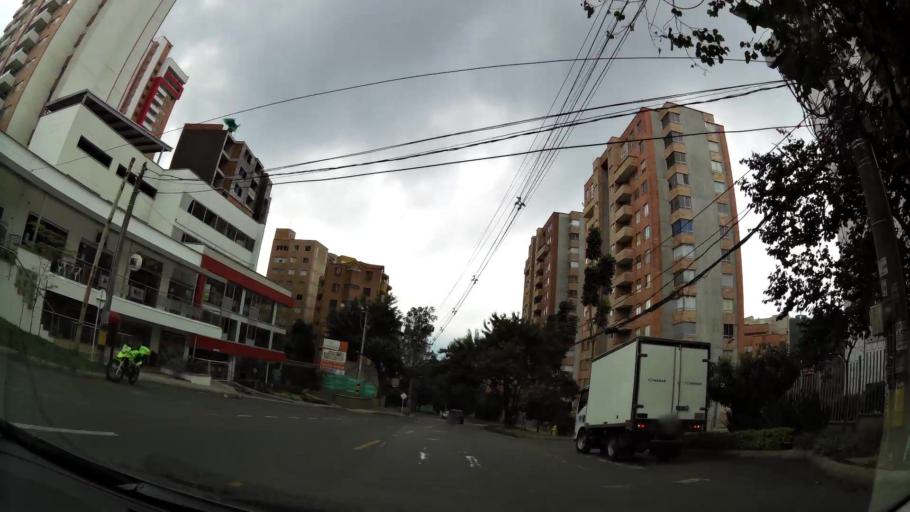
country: CO
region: Antioquia
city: Medellin
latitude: 6.2754
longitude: -75.5840
